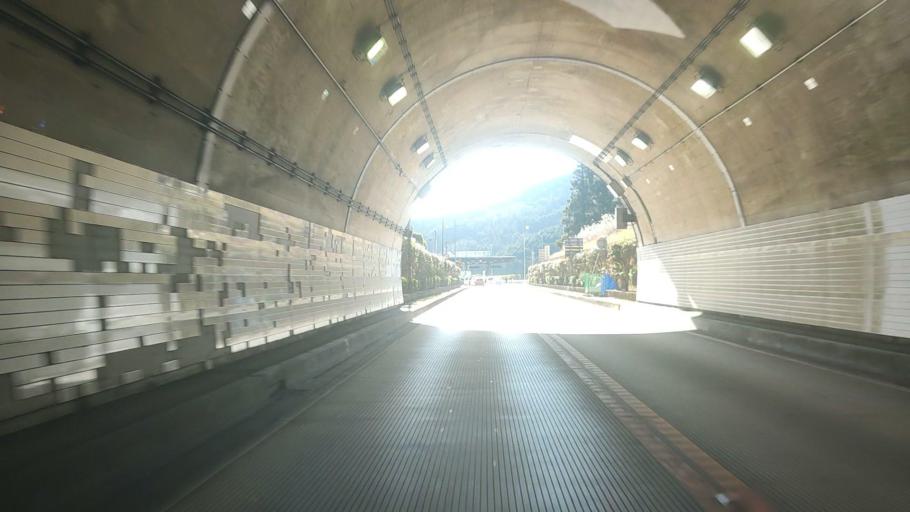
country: JP
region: Fukuoka
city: Maebaru-chuo
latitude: 33.4647
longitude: 130.2771
